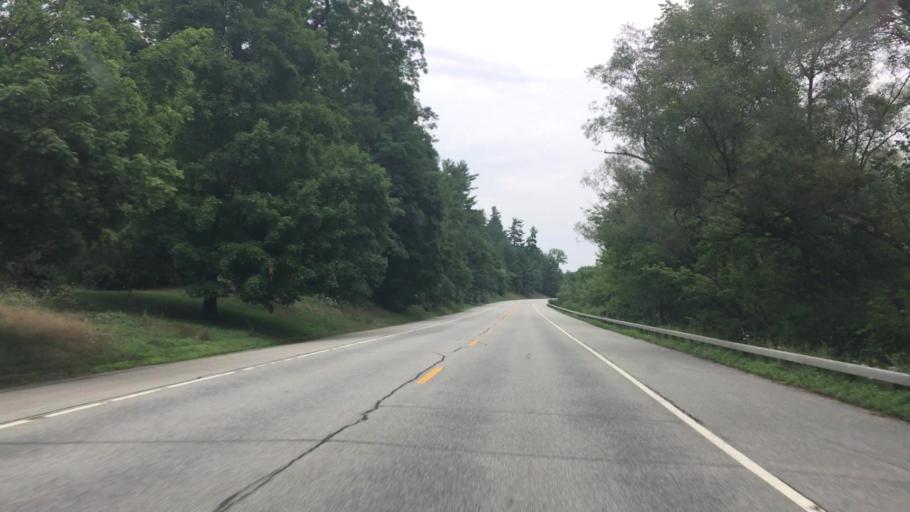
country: US
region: New York
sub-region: Essex County
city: Elizabethtown
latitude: 44.3440
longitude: -73.7667
